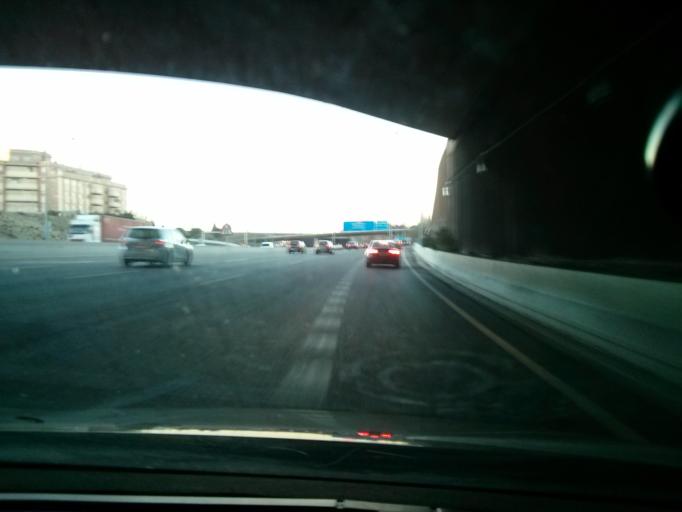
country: ES
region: Madrid
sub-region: Provincia de Madrid
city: Pozuelo de Alarcon
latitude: 40.4672
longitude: -3.7922
